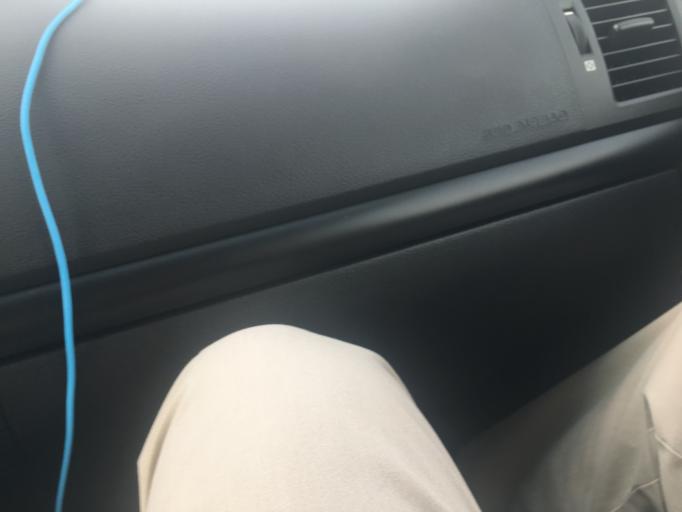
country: TM
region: Ahal
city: Kaka
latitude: 37.3947
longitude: 59.5671
